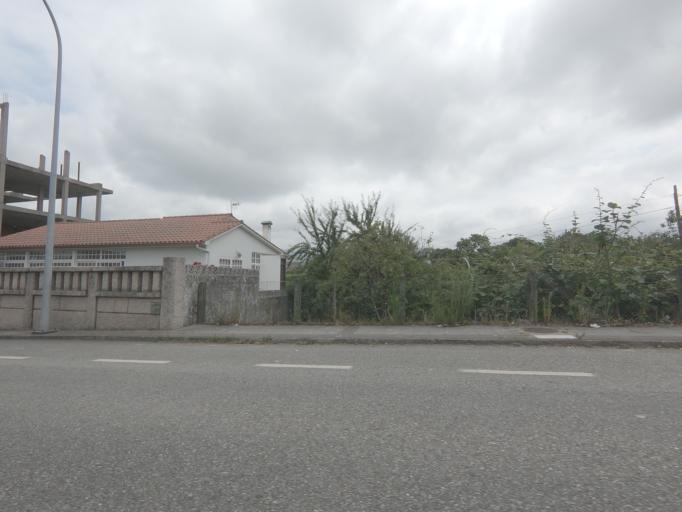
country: PT
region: Viana do Castelo
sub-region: Vila Nova de Cerveira
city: Vila Nova de Cerveira
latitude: 41.9466
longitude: -8.7765
